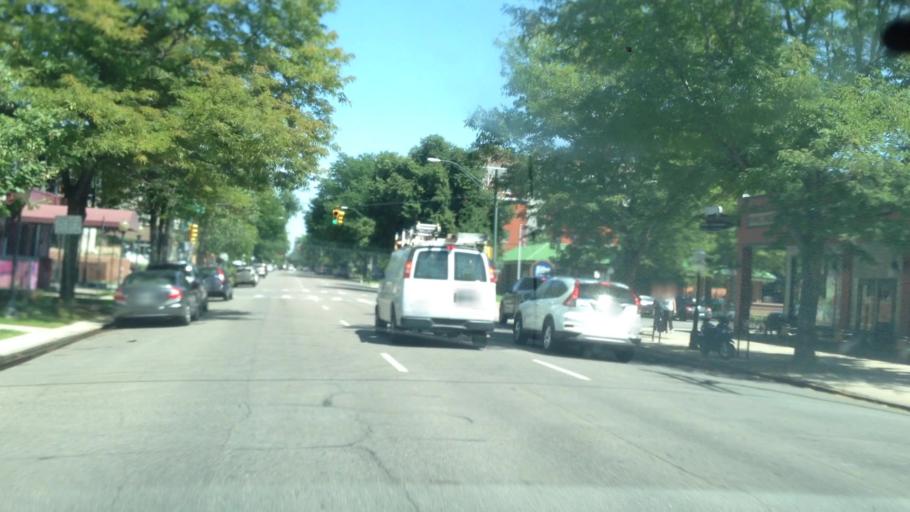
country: US
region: Colorado
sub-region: Denver County
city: Denver
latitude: 39.7433
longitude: -104.9784
